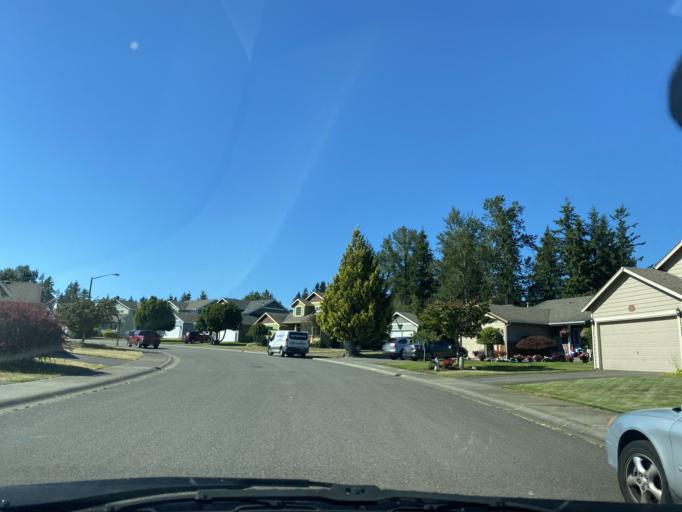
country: US
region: Washington
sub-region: Pierce County
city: South Hill
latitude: 47.1010
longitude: -122.2558
